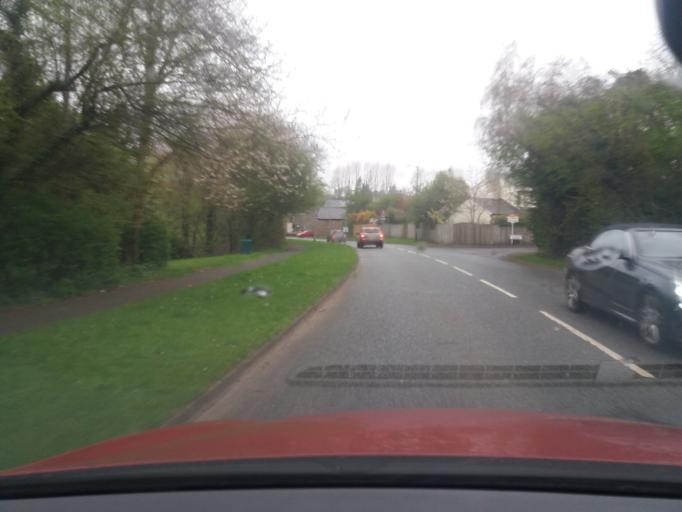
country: GB
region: England
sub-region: Lancashire
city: Clayton-le-Woods
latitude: 53.7030
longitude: -2.6352
